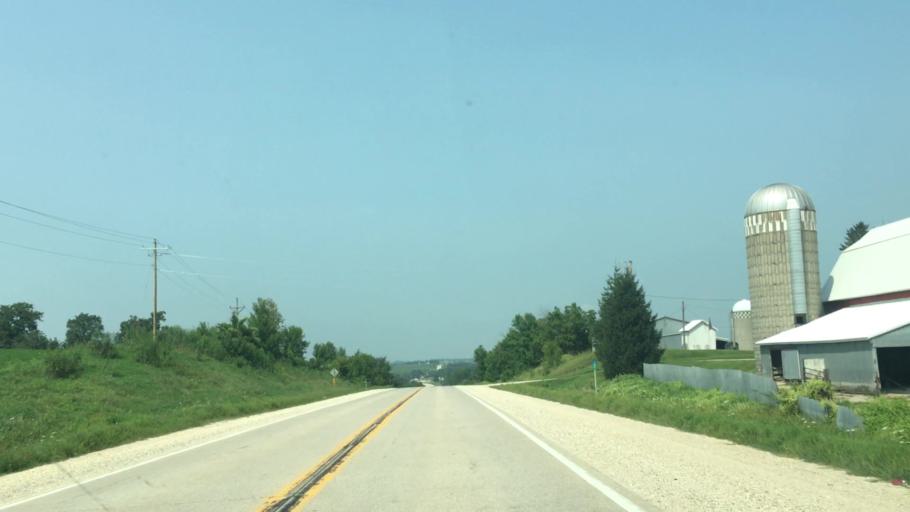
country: US
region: Iowa
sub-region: Fayette County
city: West Union
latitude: 43.1026
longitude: -91.8691
